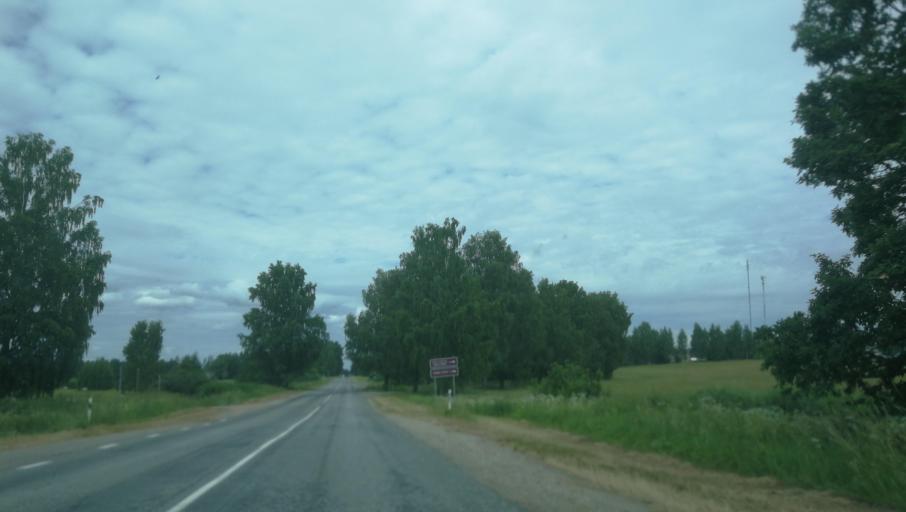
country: LV
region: Valmieras Rajons
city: Valmiera
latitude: 57.7128
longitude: 25.4249
